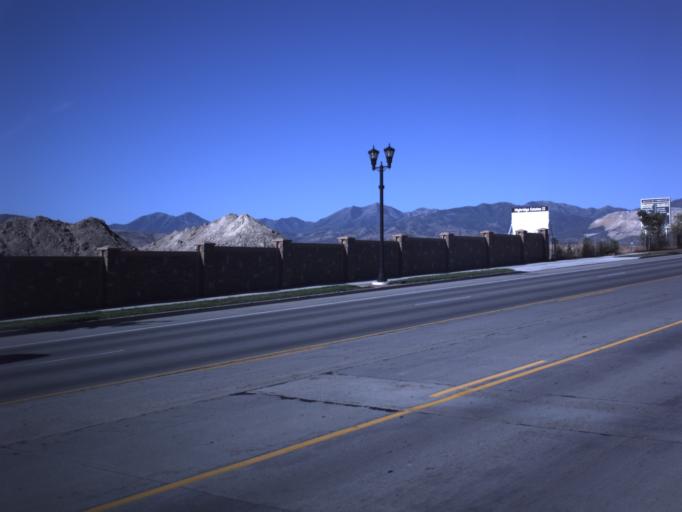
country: US
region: Utah
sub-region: Salt Lake County
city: South Jordan Heights
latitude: 40.5442
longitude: -111.9738
